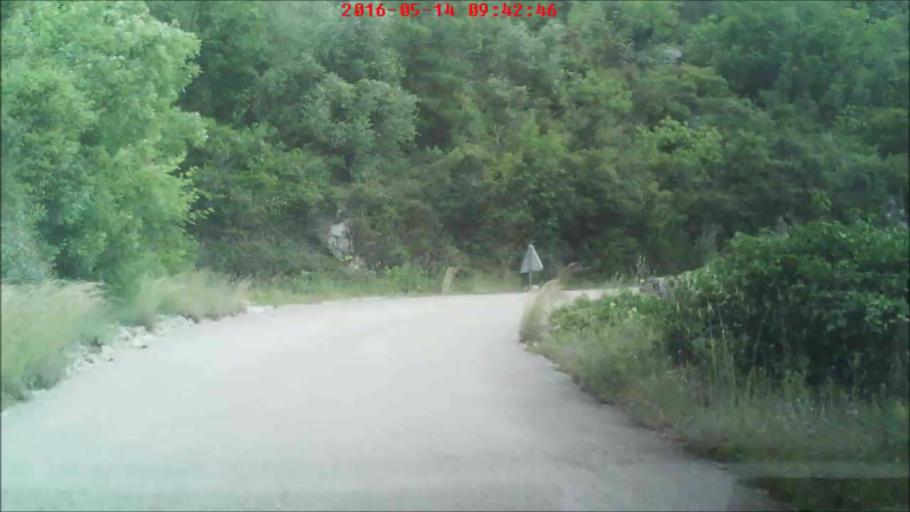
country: HR
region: Dubrovacko-Neretvanska
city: Podgora
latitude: 42.7883
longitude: 17.9037
